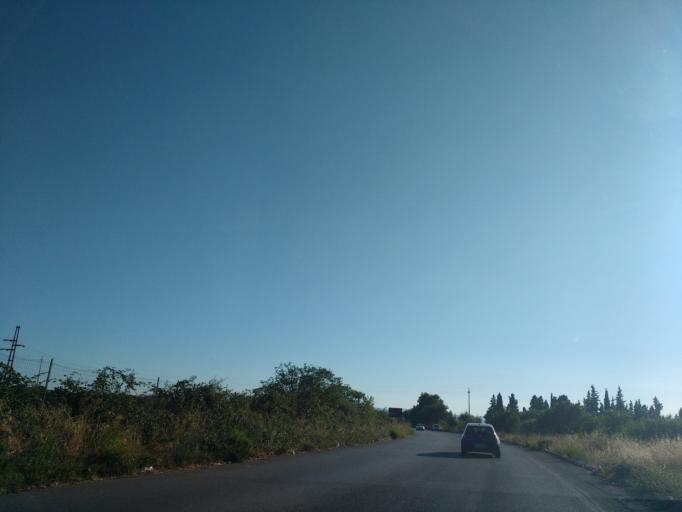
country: IT
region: Sicily
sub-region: Provincia di Siracusa
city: Siracusa
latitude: 37.0646
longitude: 15.2451
